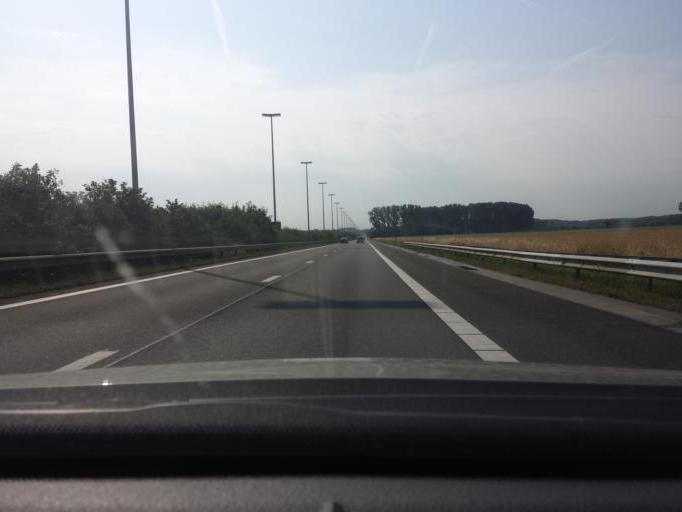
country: BE
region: Flanders
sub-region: Provincie Limburg
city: Diepenbeek
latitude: 50.8870
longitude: 5.4441
